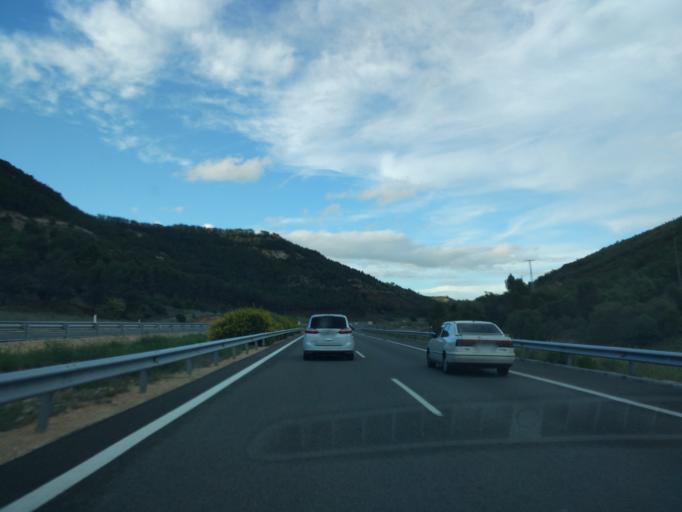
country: ES
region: Castille-La Mancha
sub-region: Provincia de Guadalajara
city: Aldeanueva de Guadalajara
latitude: 40.7096
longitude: -3.0725
